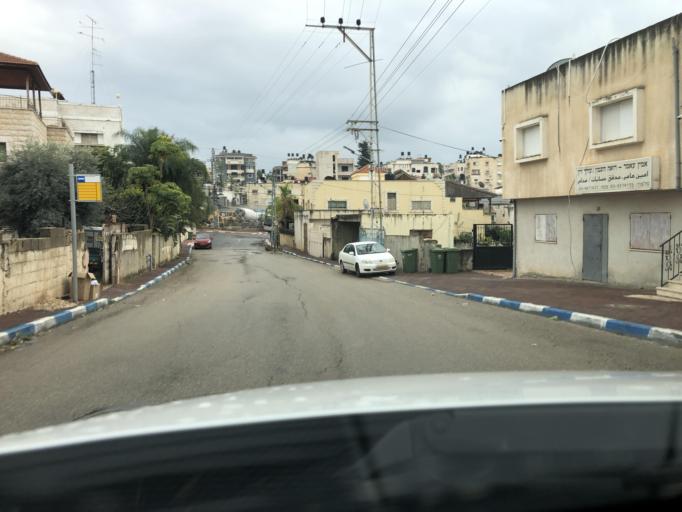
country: IL
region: Central District
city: Kafr Qasim
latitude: 32.1124
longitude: 34.9752
